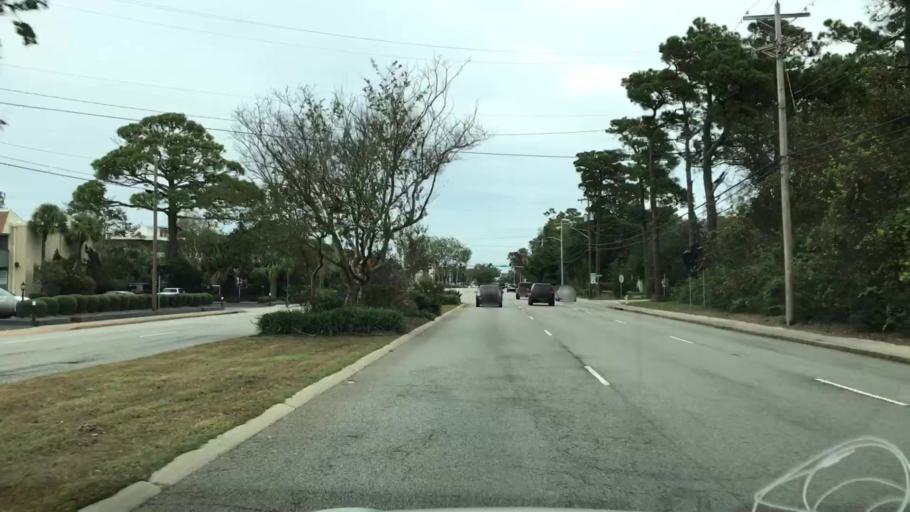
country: US
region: South Carolina
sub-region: Horry County
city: Myrtle Beach
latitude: 33.7214
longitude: -78.8493
